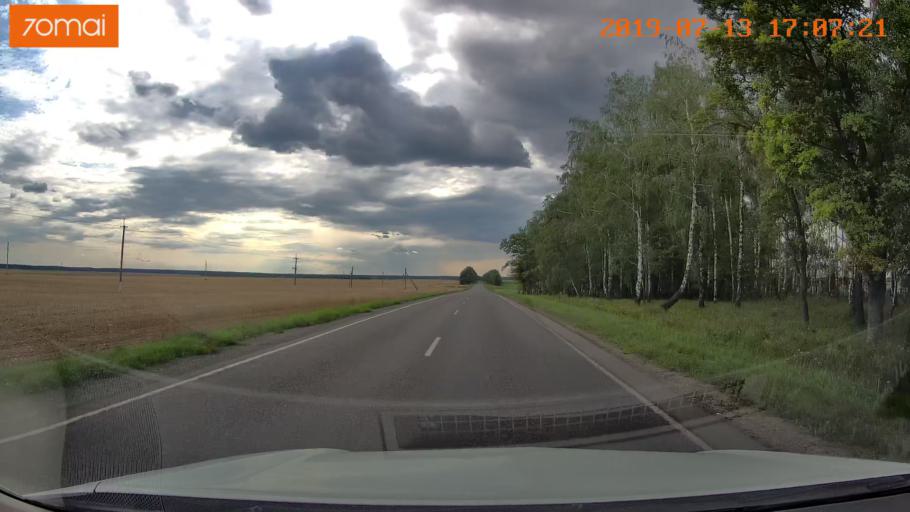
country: BY
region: Mogilev
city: Kirawsk
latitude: 53.2681
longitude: 29.3327
